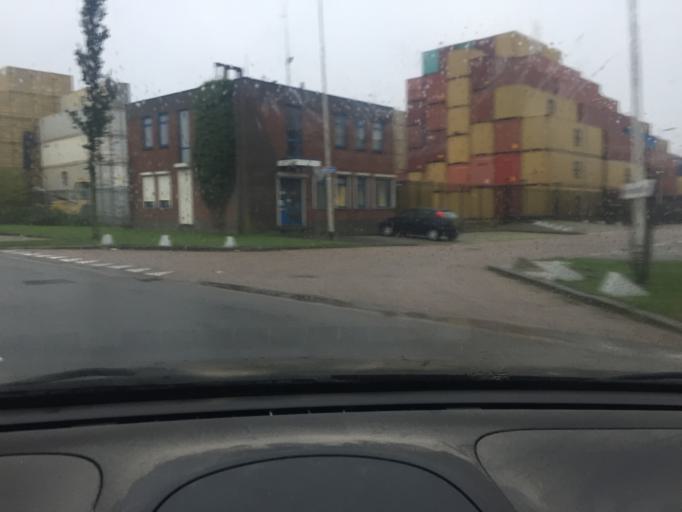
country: NL
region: South Holland
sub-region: Gemeente Albrandswaard
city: Rhoon
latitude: 51.8917
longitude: 4.4131
